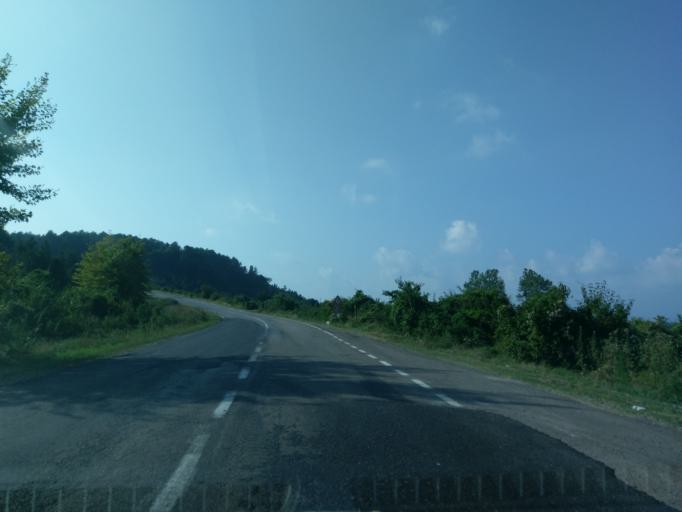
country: TR
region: Sinop
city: Yenikonak
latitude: 41.9407
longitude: 34.7191
